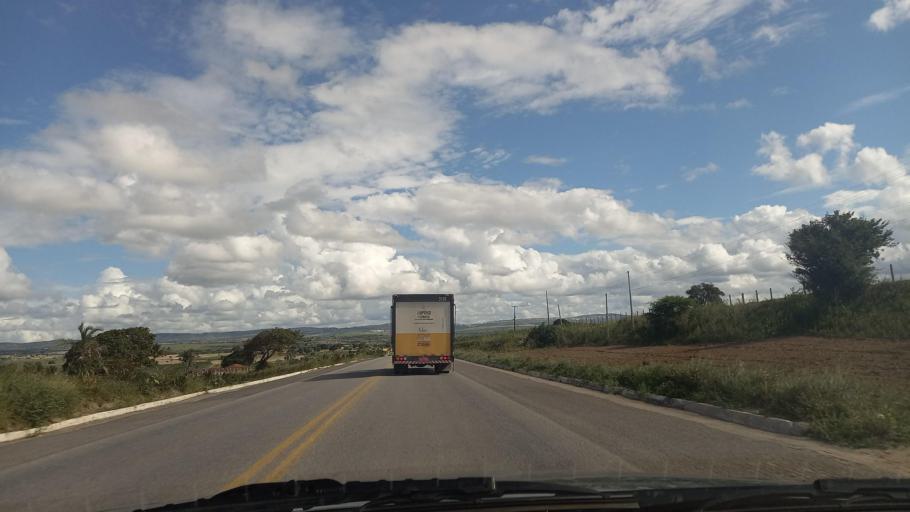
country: BR
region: Pernambuco
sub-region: Sao Joao
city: Sao Joao
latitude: -8.7757
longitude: -36.4279
